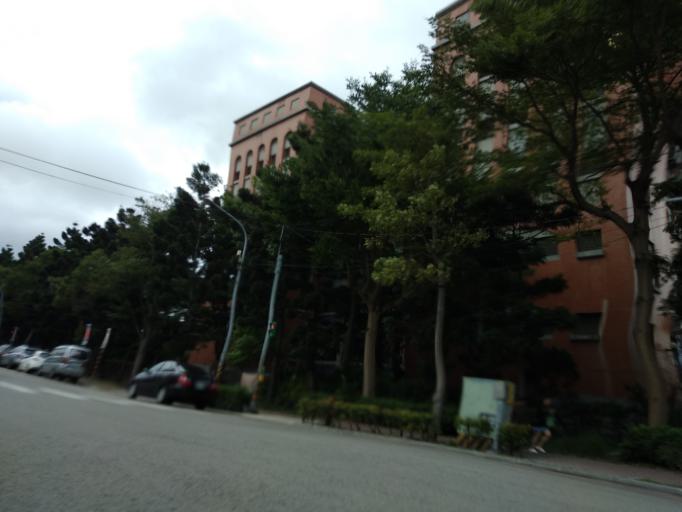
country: TW
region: Taiwan
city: Taoyuan City
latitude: 24.9616
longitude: 121.2111
